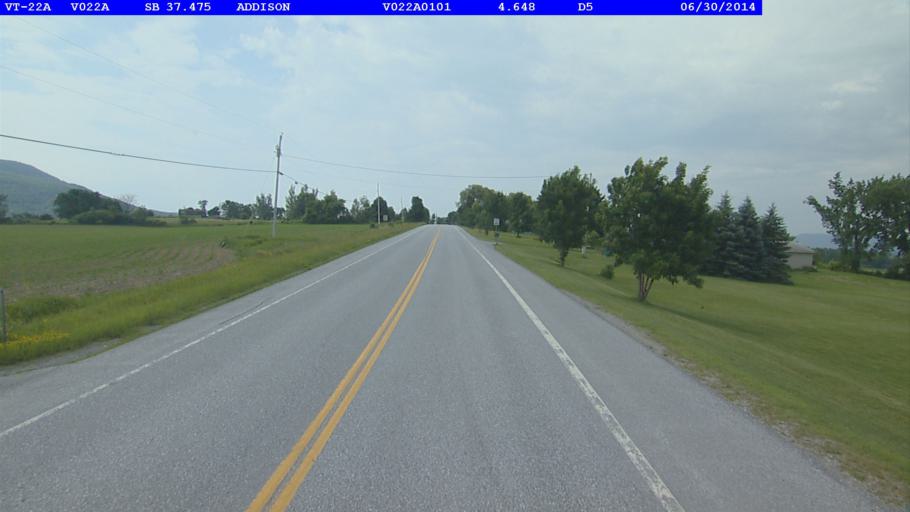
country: US
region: Vermont
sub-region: Addison County
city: Vergennes
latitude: 44.0963
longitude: -73.3002
